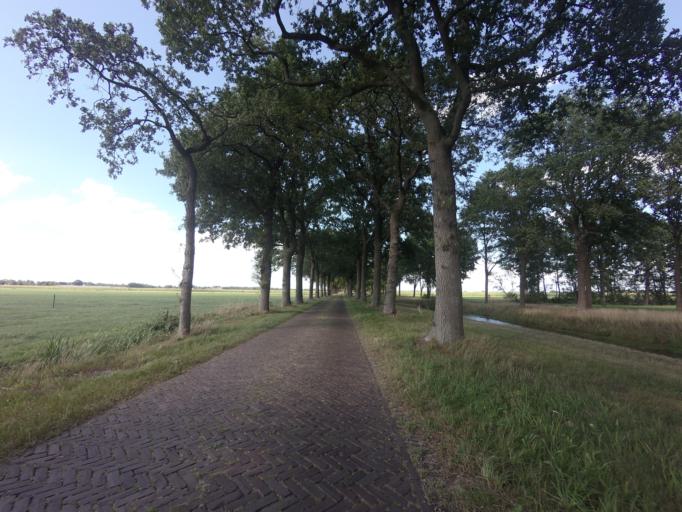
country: NL
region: Drenthe
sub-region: Gemeente Hoogeveen
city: Hoogeveen
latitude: 52.6544
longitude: 6.5143
